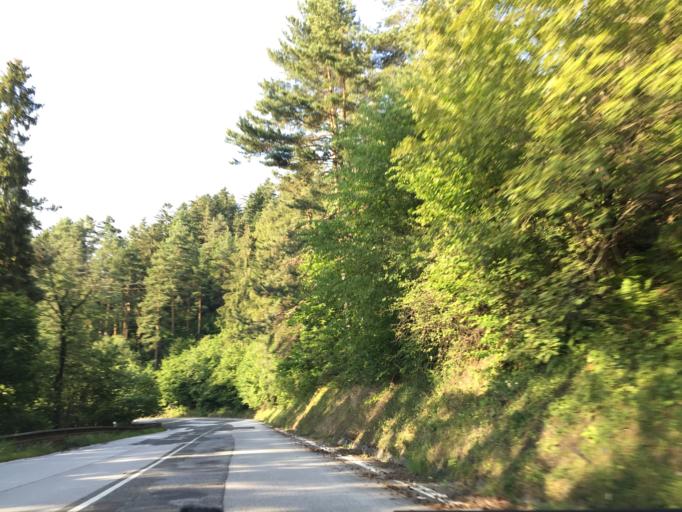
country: SK
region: Presovsky
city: Spisske Podhradie
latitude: 49.0123
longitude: 20.8517
